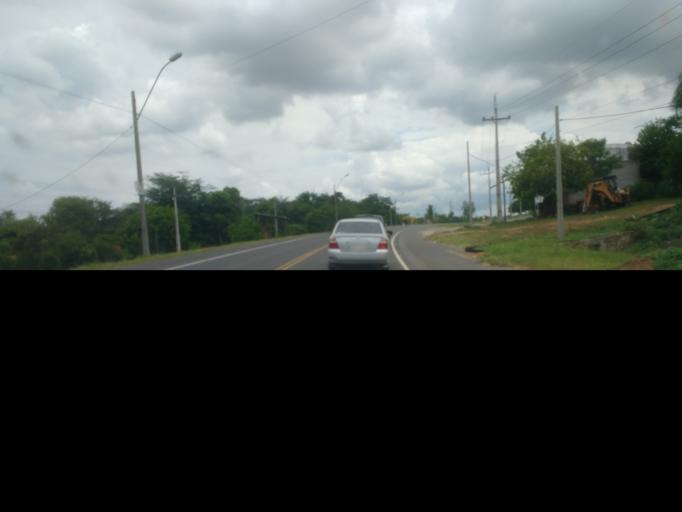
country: PY
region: Central
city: Limpio
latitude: -25.1343
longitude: -57.4485
